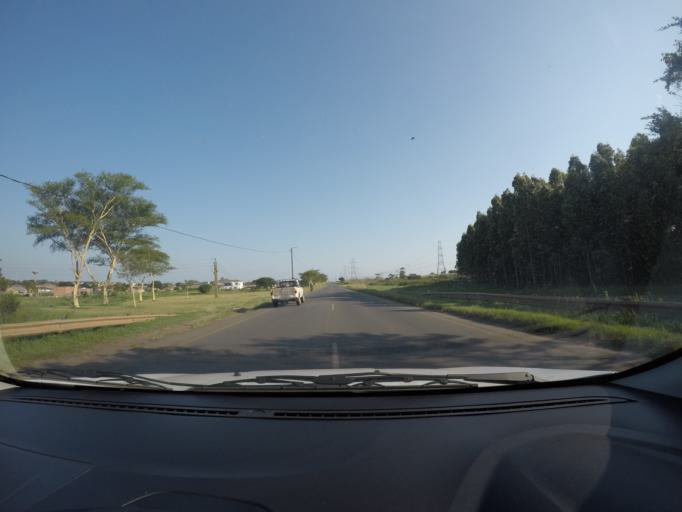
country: ZA
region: KwaZulu-Natal
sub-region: uThungulu District Municipality
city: Richards Bay
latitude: -28.7209
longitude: 32.0334
